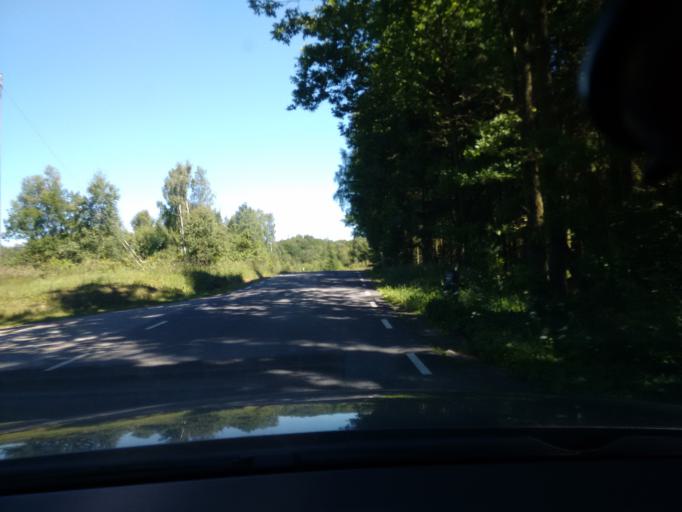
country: SE
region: Skane
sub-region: Kristianstads Kommun
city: Degeberga
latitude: 55.7810
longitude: 14.0561
